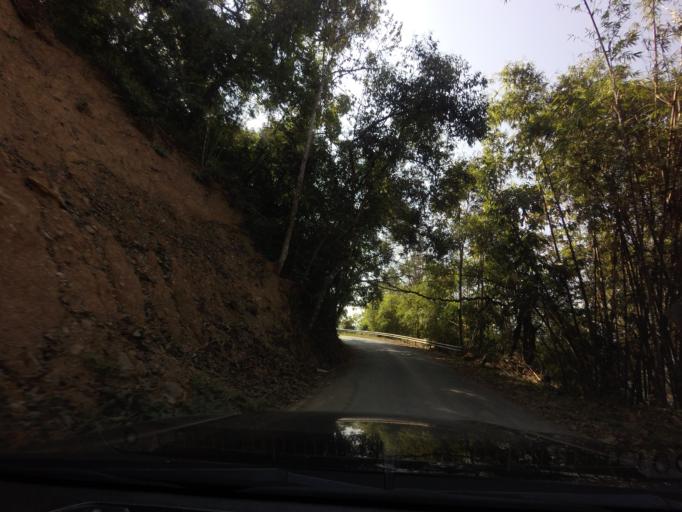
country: TH
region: Kanchanaburi
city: Thong Pha Phum
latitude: 14.6904
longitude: 98.4551
